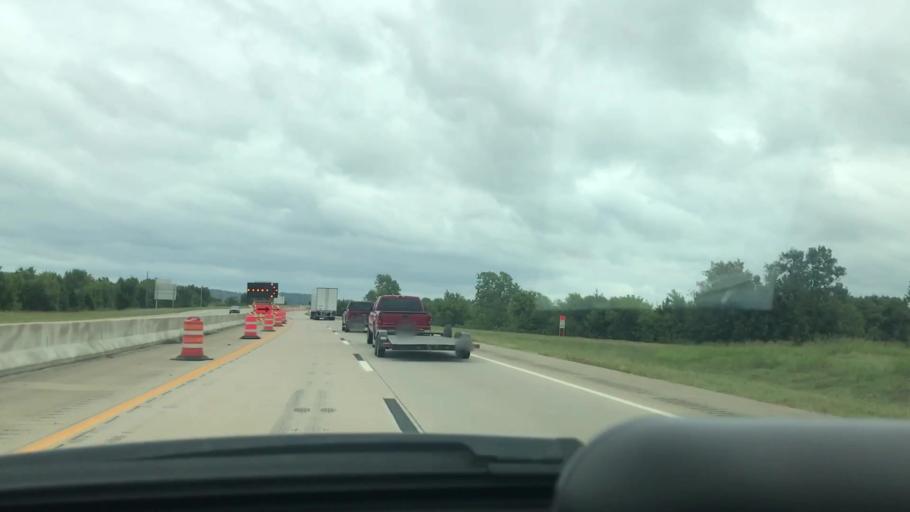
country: US
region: Oklahoma
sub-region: McIntosh County
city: Eufaula
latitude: 35.2169
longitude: -95.6105
